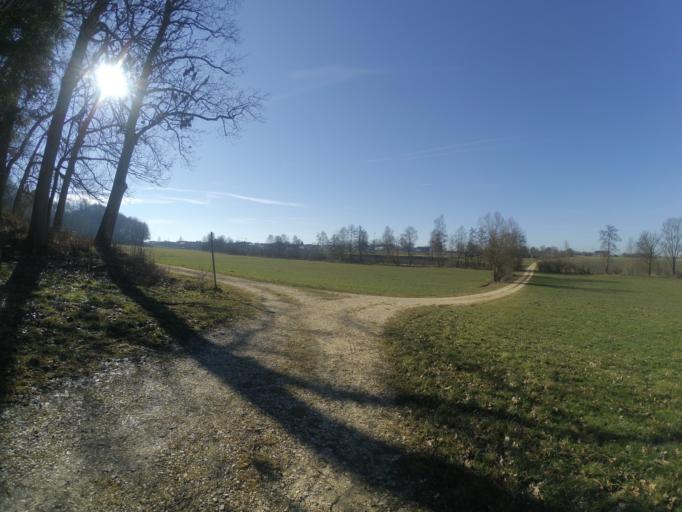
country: DE
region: Baden-Wuerttemberg
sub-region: Tuebingen Region
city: Huttisheim
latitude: 48.2876
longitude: 9.9408
